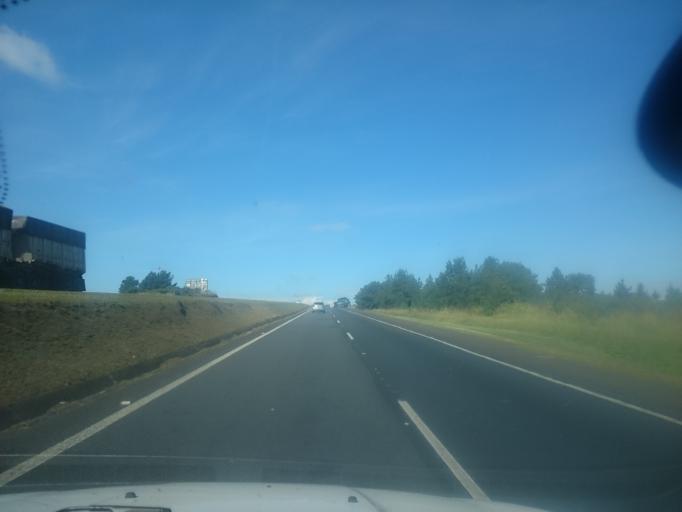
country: BR
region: Parana
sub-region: Palmeira
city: Palmeira
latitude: -25.3667
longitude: -49.8232
